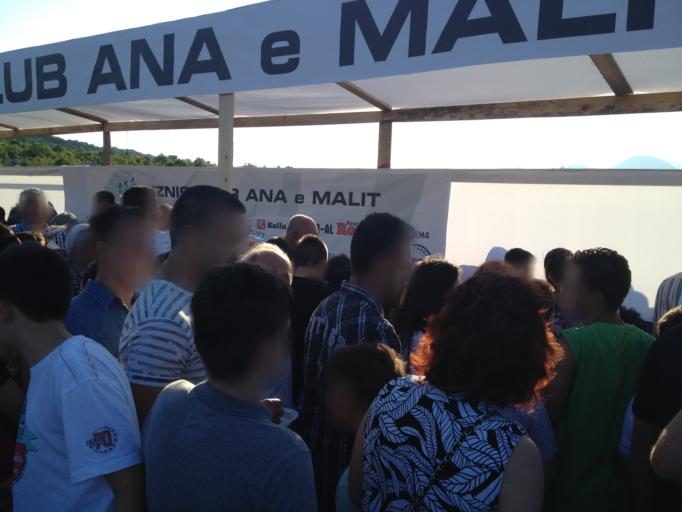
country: AL
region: Shkoder
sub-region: Rrethi i Shkodres
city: Dajc
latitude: 41.9902
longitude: 19.3168
